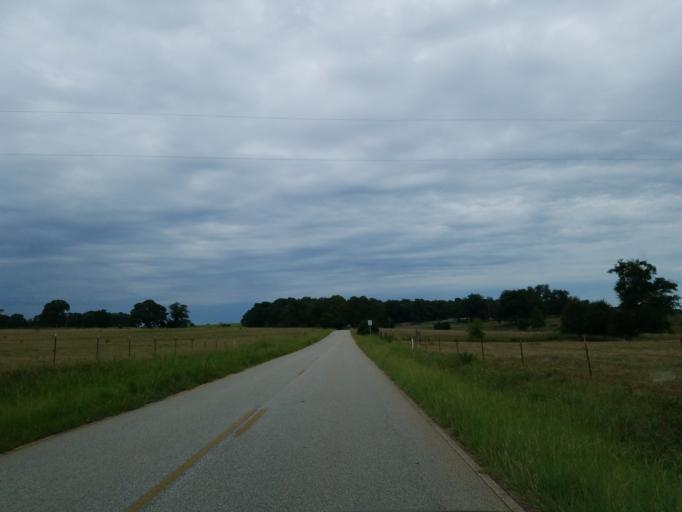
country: US
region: Georgia
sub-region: Monroe County
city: Forsyth
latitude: 32.9886
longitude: -84.0334
